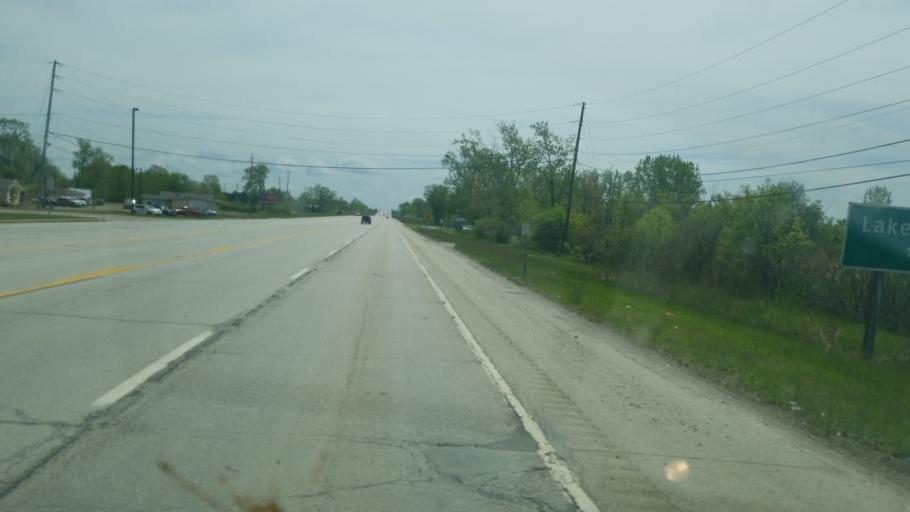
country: US
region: Ohio
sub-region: Ottawa County
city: Port Clinton
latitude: 41.5287
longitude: -83.0167
